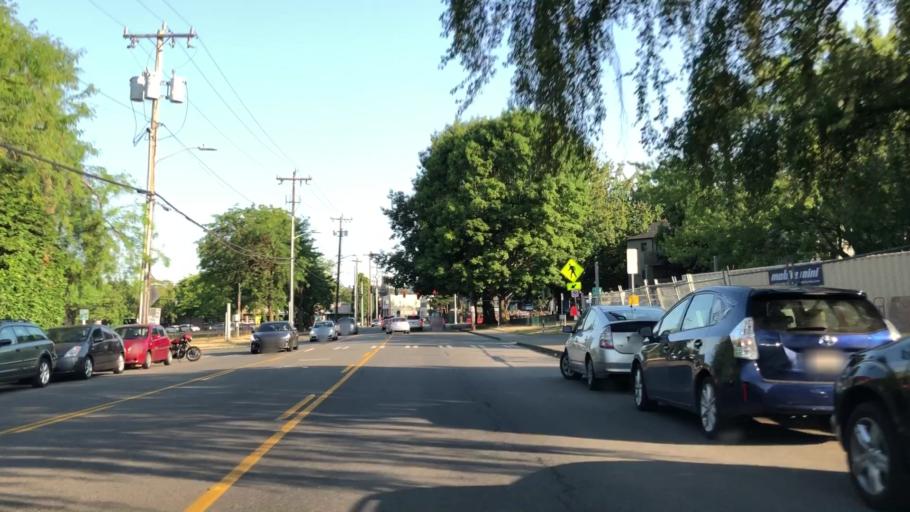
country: US
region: Washington
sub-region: King County
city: Seattle
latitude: 47.6600
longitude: -122.2918
